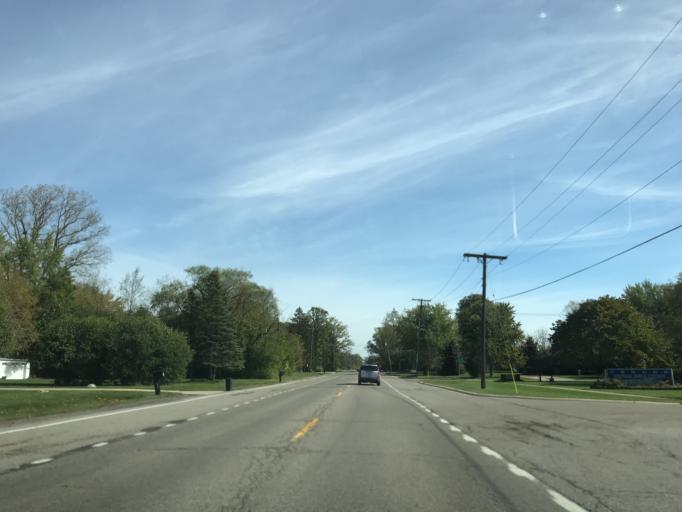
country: US
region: Michigan
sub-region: Oakland County
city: Farmington
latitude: 42.4709
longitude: -83.3263
